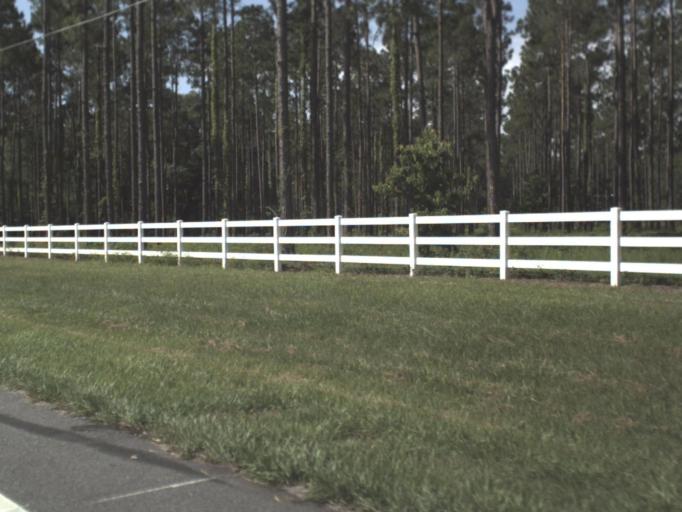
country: US
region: Florida
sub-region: Madison County
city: Madison
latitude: 30.4110
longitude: -83.3691
